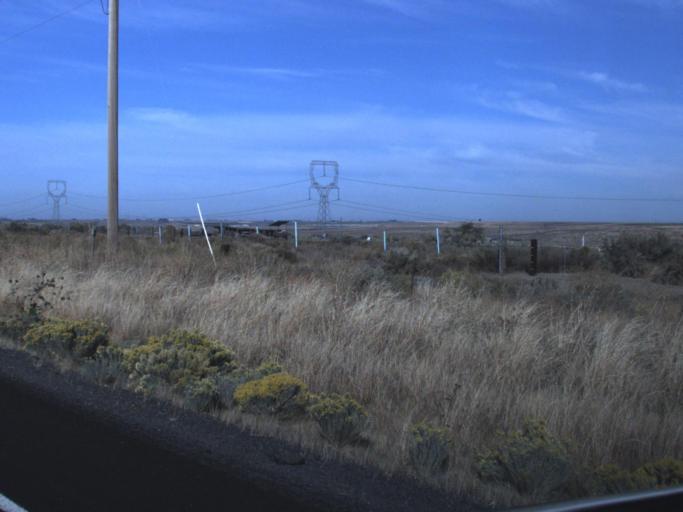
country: US
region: Washington
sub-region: Franklin County
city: Connell
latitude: 46.6346
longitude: -118.7692
